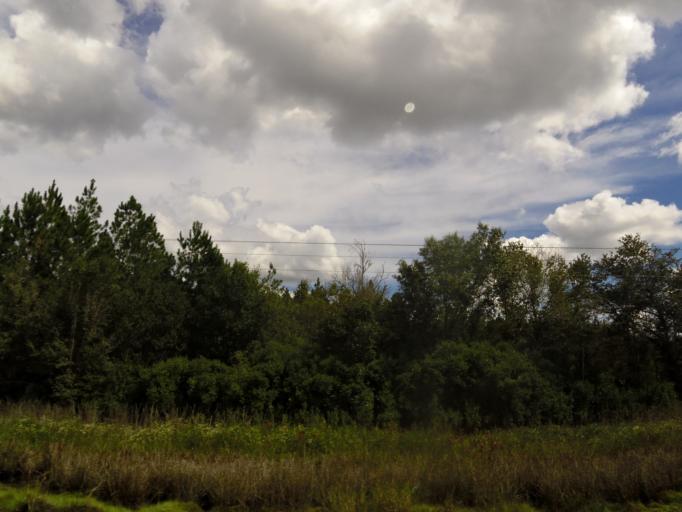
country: US
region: Georgia
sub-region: Brantley County
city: Nahunta
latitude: 31.1473
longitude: -81.9916
